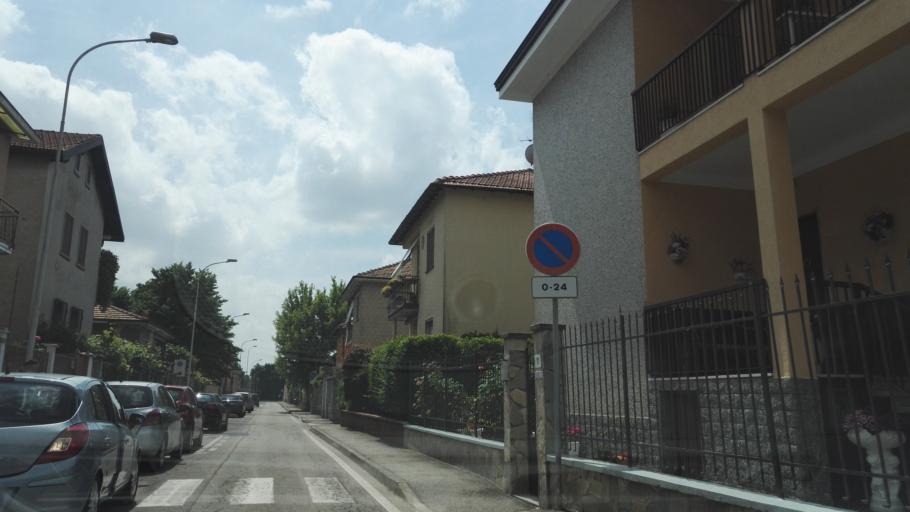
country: IT
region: Lombardy
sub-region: Citta metropolitana di Milano
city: Mezzate
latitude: 45.4390
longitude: 9.2944
